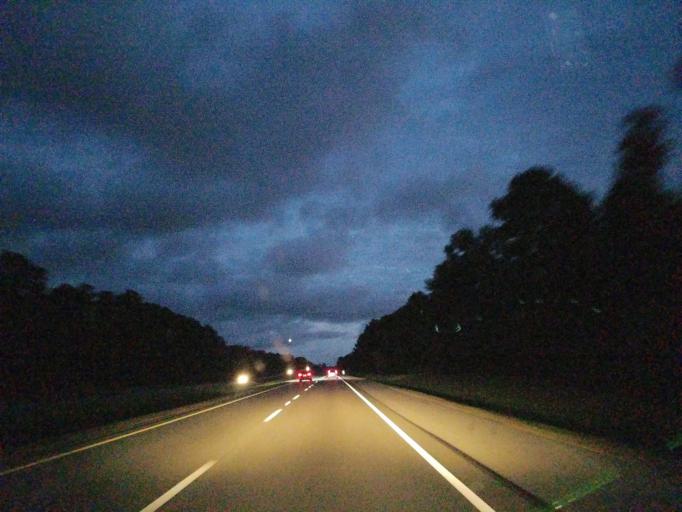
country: US
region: Mississippi
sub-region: Jones County
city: Sharon
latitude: 31.8347
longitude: -89.0503
